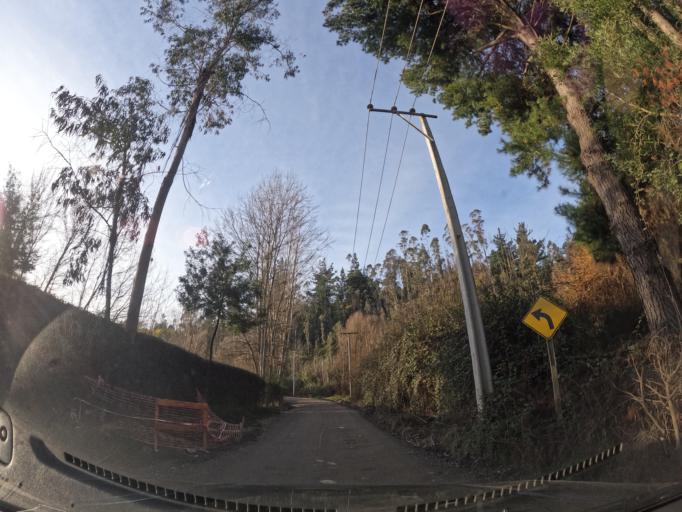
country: CL
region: Biobio
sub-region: Provincia de Concepcion
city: Concepcion
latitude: -36.8611
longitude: -72.9975
